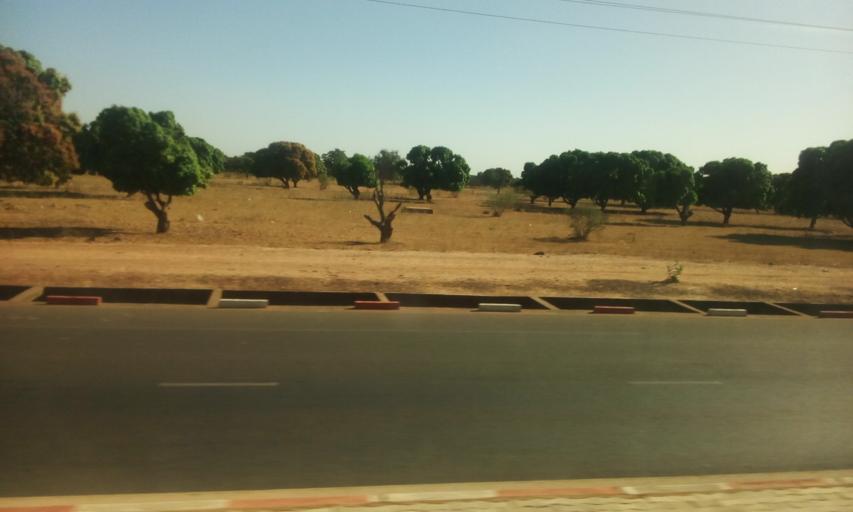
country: ML
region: Segou
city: Segou
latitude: 13.4205
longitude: -6.2982
